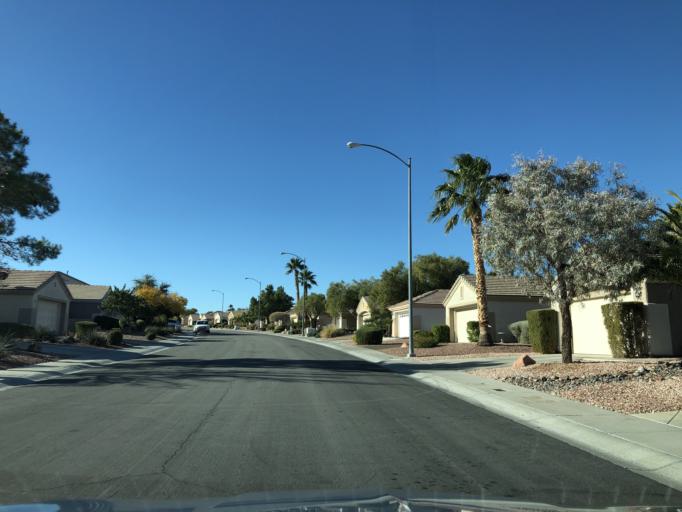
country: US
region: Nevada
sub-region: Clark County
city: Whitney
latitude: 36.0110
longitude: -115.0749
